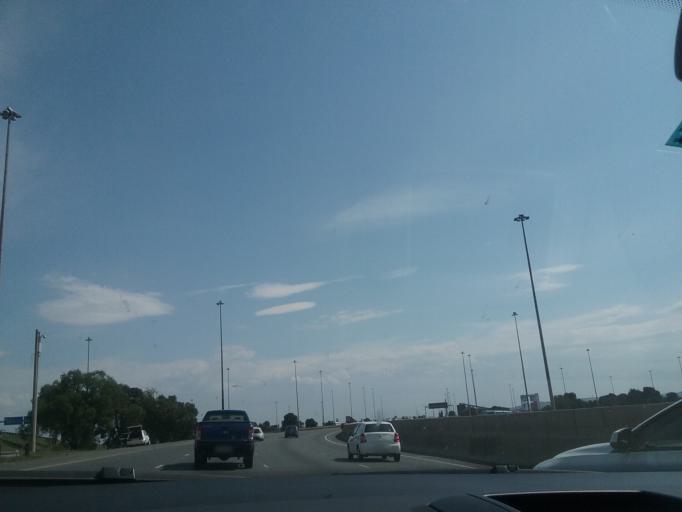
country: ZA
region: Gauteng
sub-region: Ekurhuleni Metropolitan Municipality
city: Germiston
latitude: -26.2089
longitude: 28.1367
